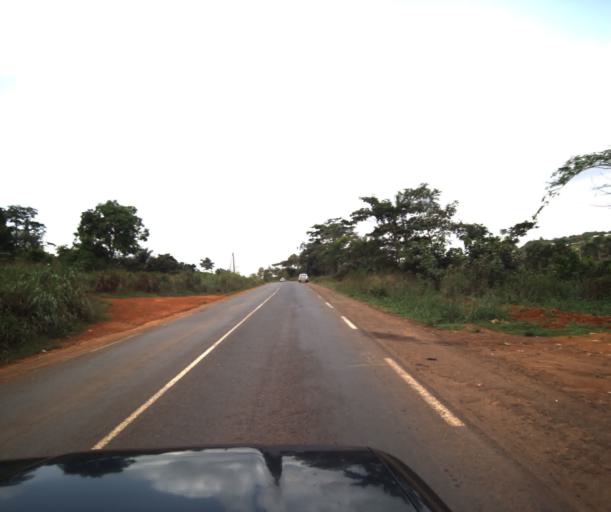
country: CM
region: Centre
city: Mbankomo
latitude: 3.7914
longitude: 11.4126
